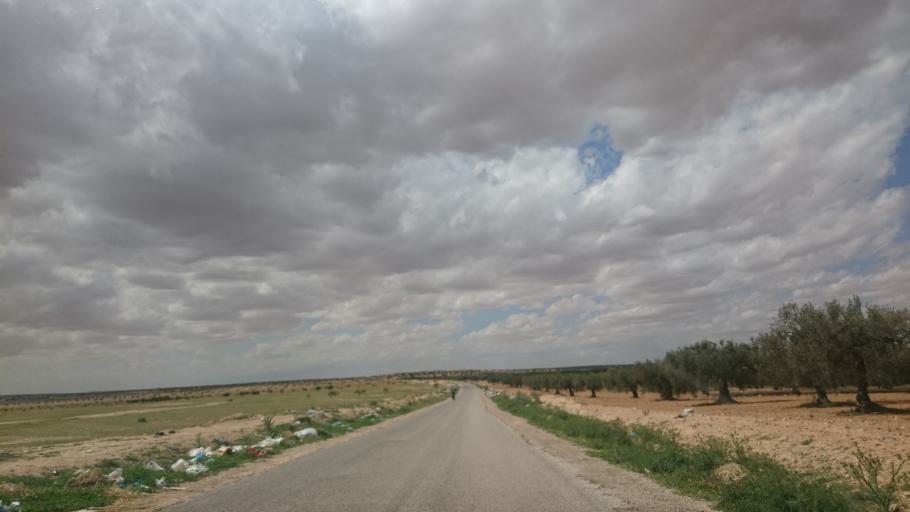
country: TN
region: Safaqis
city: Sfax
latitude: 34.7476
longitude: 10.5106
